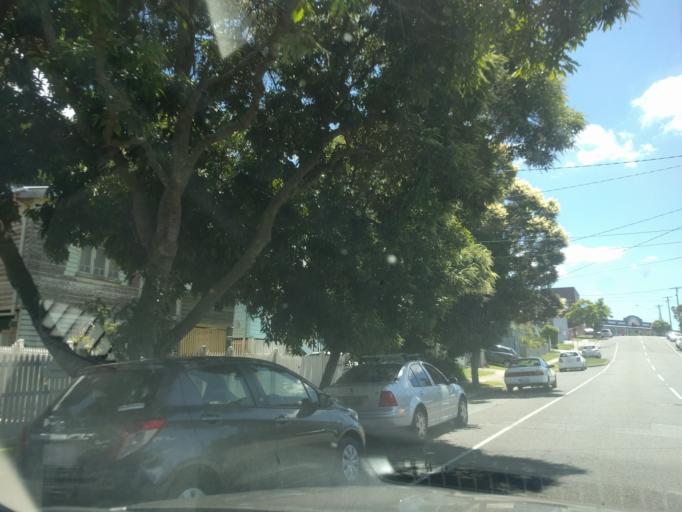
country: AU
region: Queensland
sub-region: Brisbane
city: Milton
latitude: -27.4624
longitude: 153.0048
